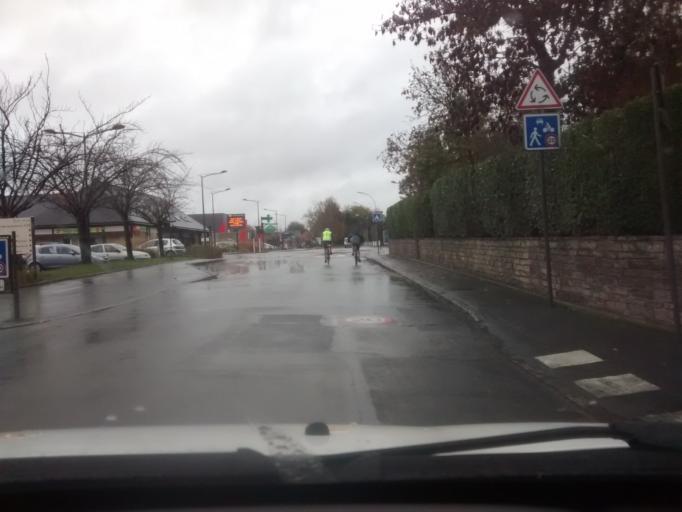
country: FR
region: Brittany
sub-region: Departement d'Ille-et-Vilaine
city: Fouillard
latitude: 48.1583
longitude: -1.5798
